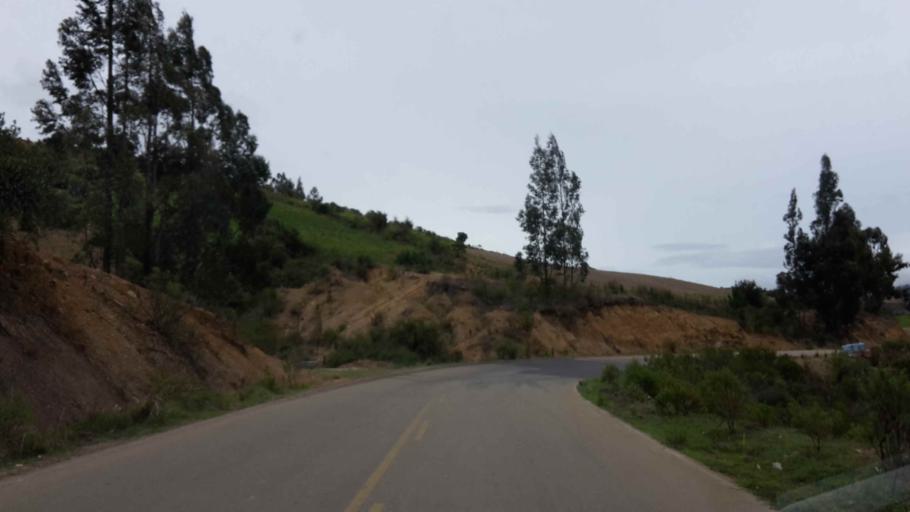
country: BO
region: Cochabamba
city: Totora
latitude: -17.7003
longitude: -65.2147
